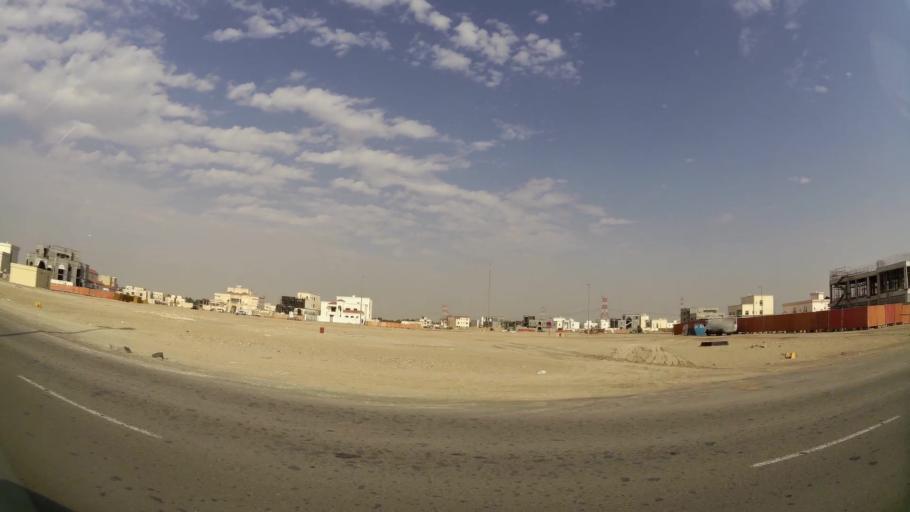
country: AE
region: Abu Dhabi
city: Abu Dhabi
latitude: 24.3327
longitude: 54.5736
